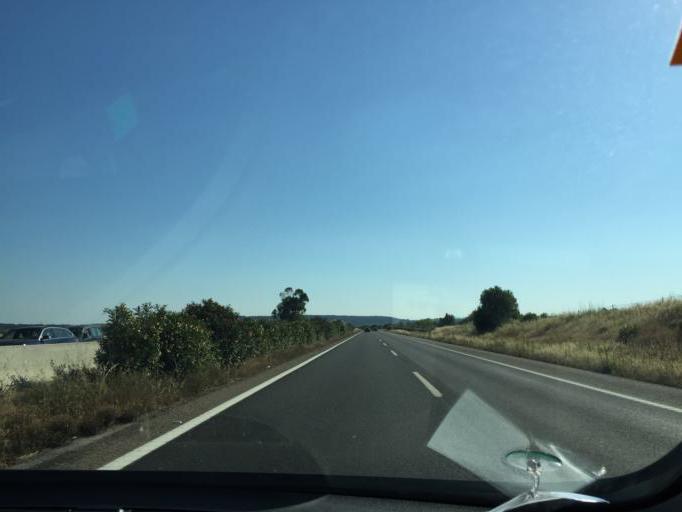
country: ES
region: Balearic Islands
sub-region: Illes Balears
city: Consell
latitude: 39.6630
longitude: 2.8132
